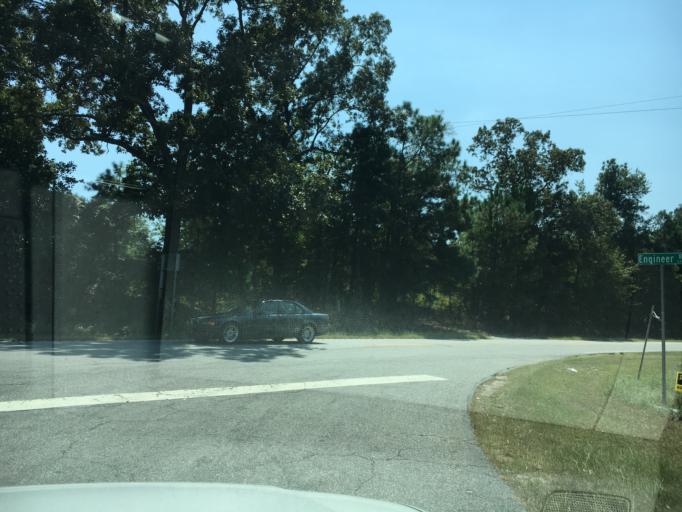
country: US
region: South Carolina
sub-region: Lexington County
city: Batesburg
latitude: 33.7993
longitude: -81.6403
